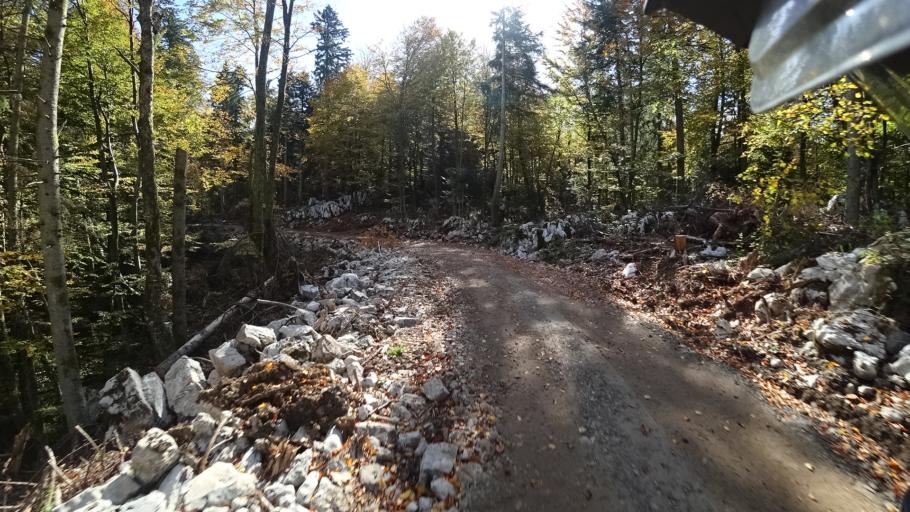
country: HR
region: Karlovacka
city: Plaski
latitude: 45.0621
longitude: 15.3460
